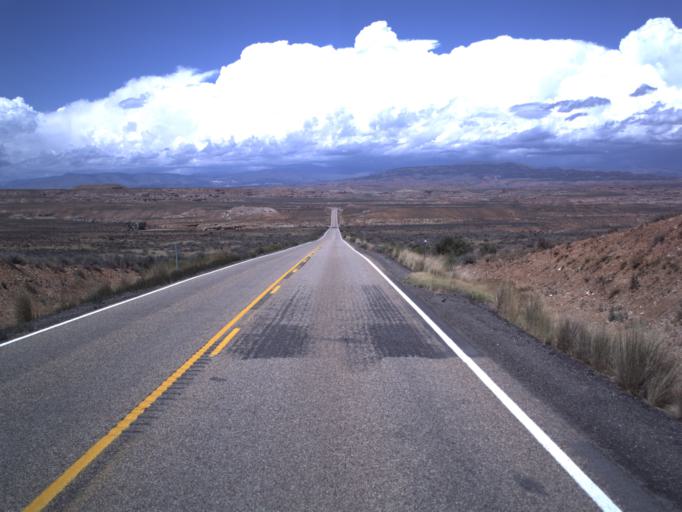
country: US
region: Utah
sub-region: Uintah County
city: Maeser
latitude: 40.2976
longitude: -109.6872
